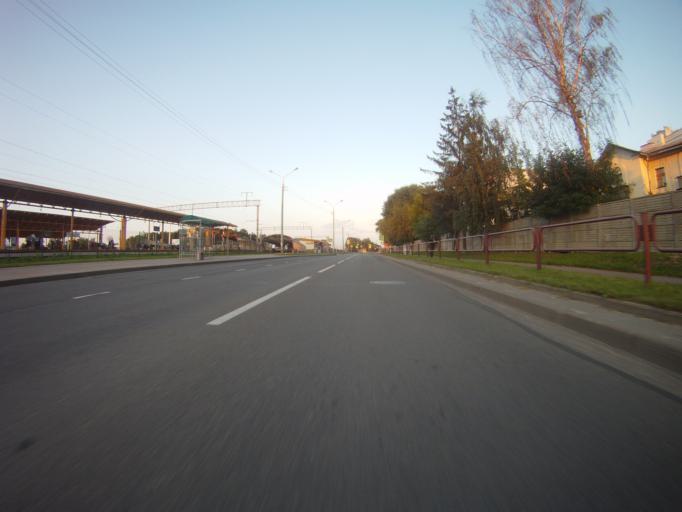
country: BY
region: Minsk
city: Zhdanovichy
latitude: 53.9299
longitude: 27.4761
